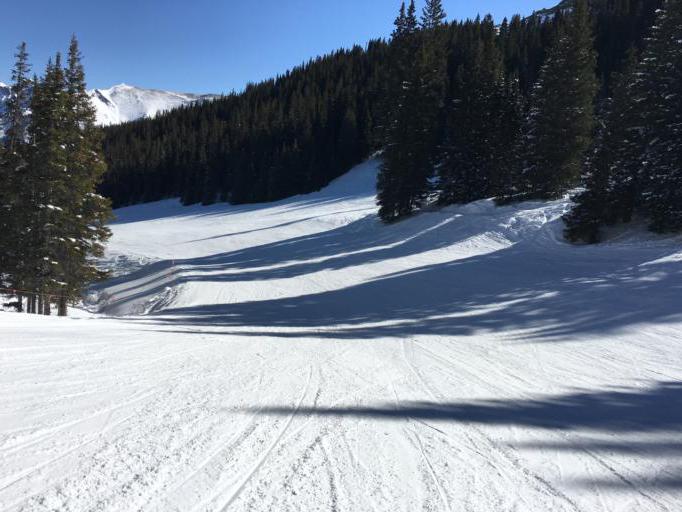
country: US
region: Colorado
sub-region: Summit County
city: Frisco
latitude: 39.4778
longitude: -106.1634
